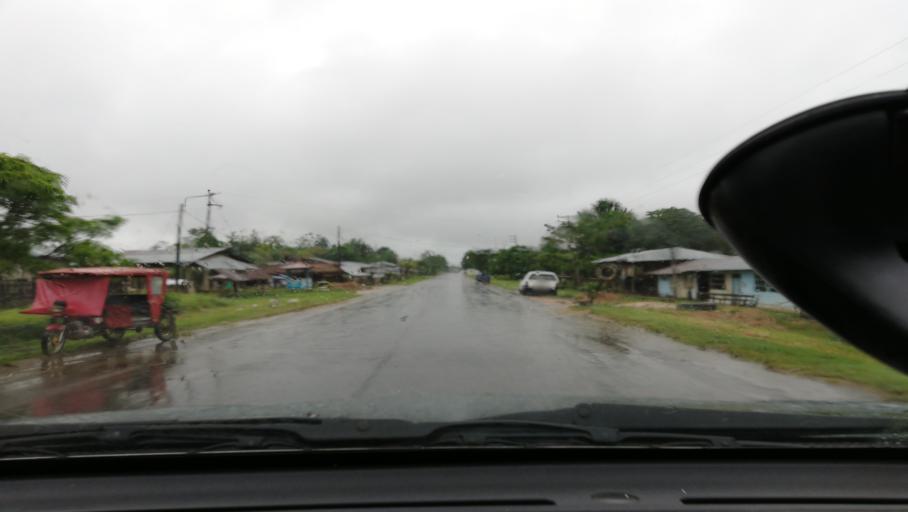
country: PE
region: Loreto
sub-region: Provincia de Maynas
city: San Juan
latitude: -4.0929
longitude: -73.4525
